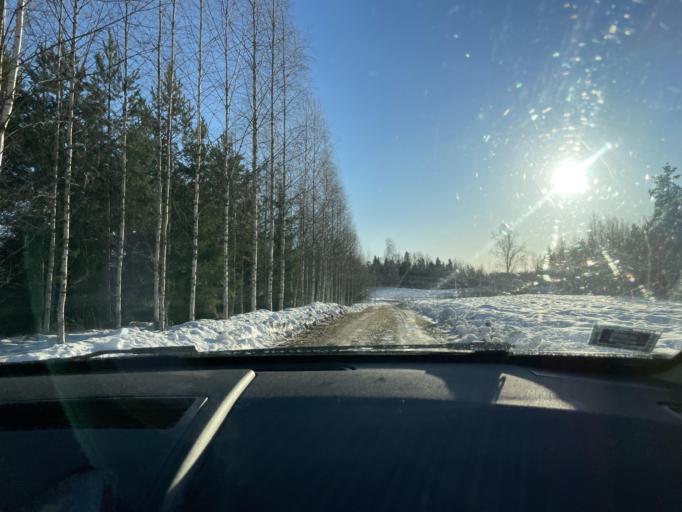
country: LV
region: Ludzas Rajons
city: Ludza
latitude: 56.4497
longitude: 27.6353
